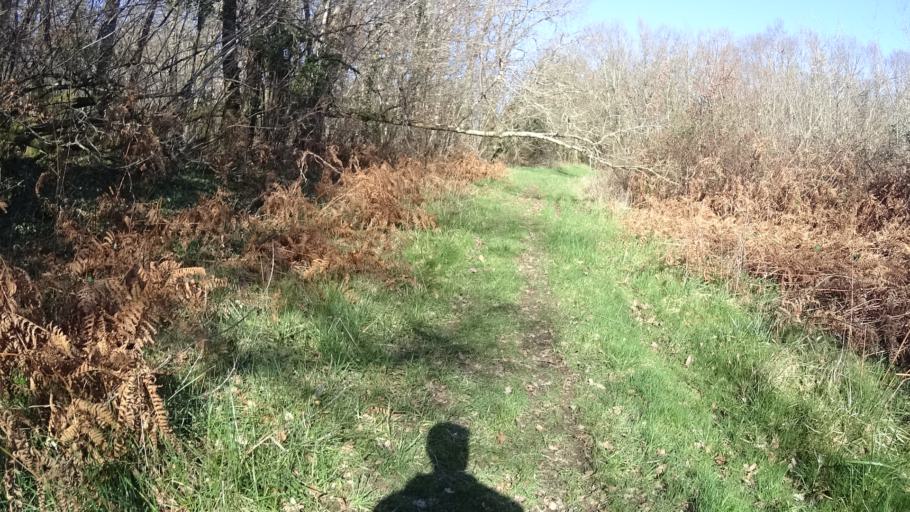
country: FR
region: Aquitaine
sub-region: Departement de la Dordogne
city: Saint-Aulaye
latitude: 45.2284
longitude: 0.1174
